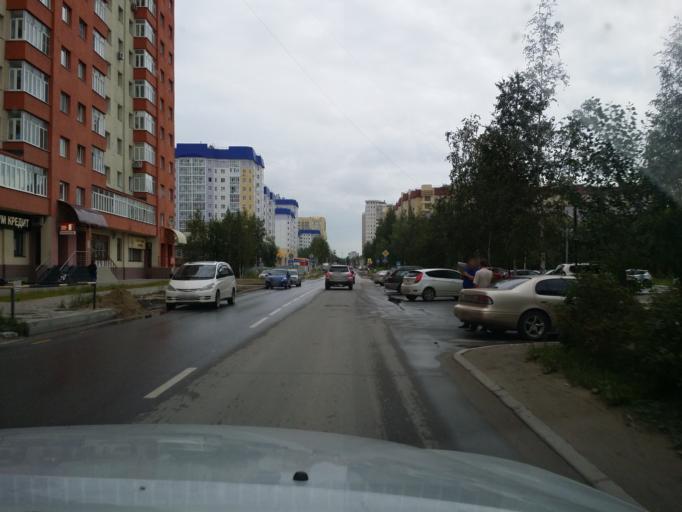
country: RU
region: Khanty-Mansiyskiy Avtonomnyy Okrug
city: Nizhnevartovsk
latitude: 60.9306
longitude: 76.5745
